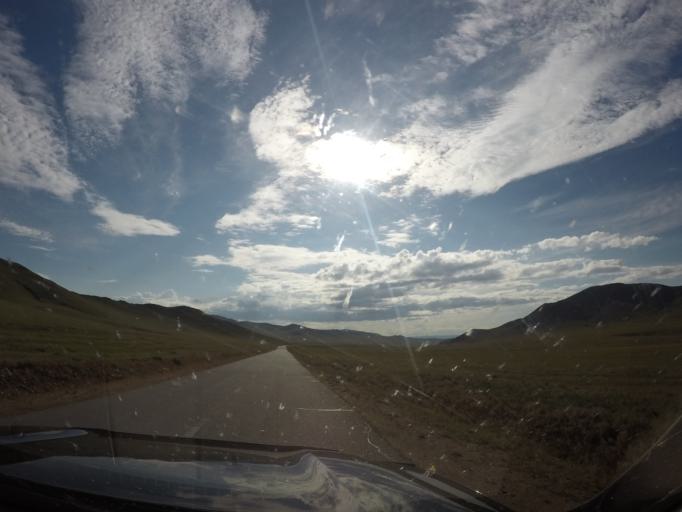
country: MN
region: Central Aimak
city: Bayandelger
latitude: 47.6977
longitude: 108.5508
